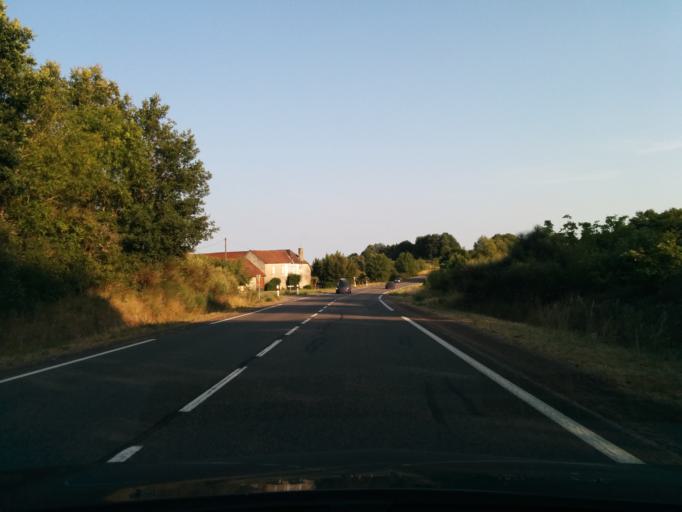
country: FR
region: Midi-Pyrenees
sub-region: Departement du Lot
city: Pradines
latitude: 44.5730
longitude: 1.4735
